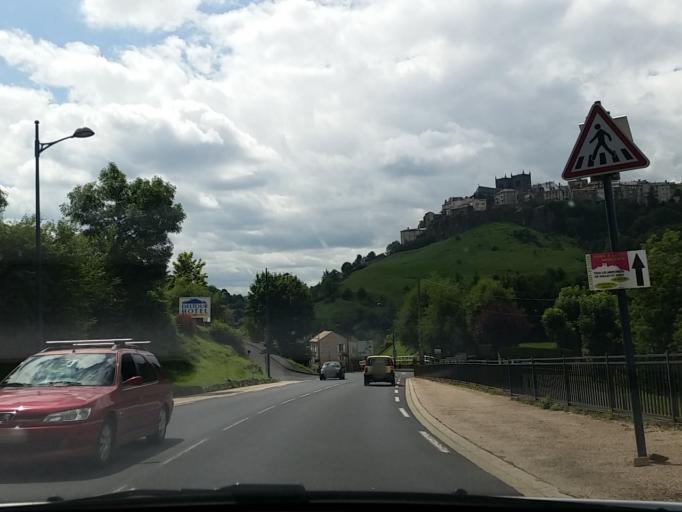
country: FR
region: Auvergne
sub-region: Departement du Cantal
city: Saint-Flour
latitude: 45.0371
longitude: 3.1013
